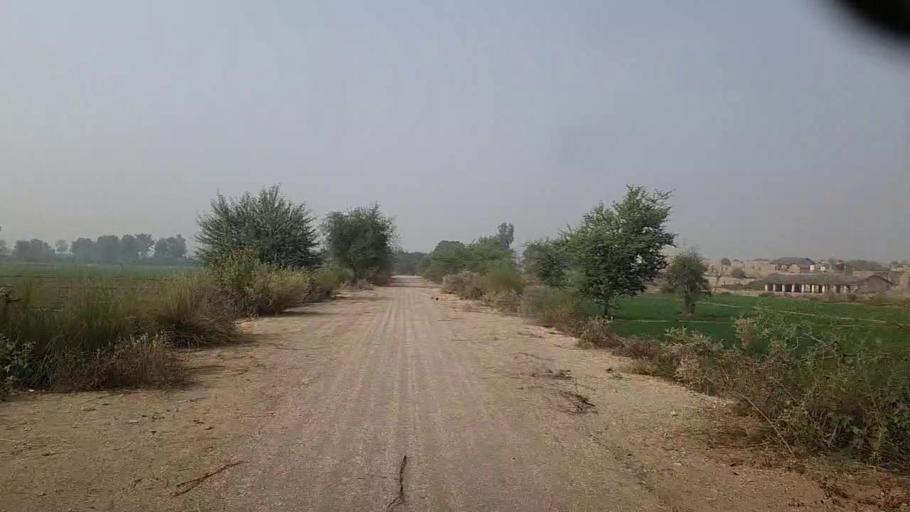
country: PK
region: Sindh
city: Kandiari
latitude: 26.9785
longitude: 68.5919
